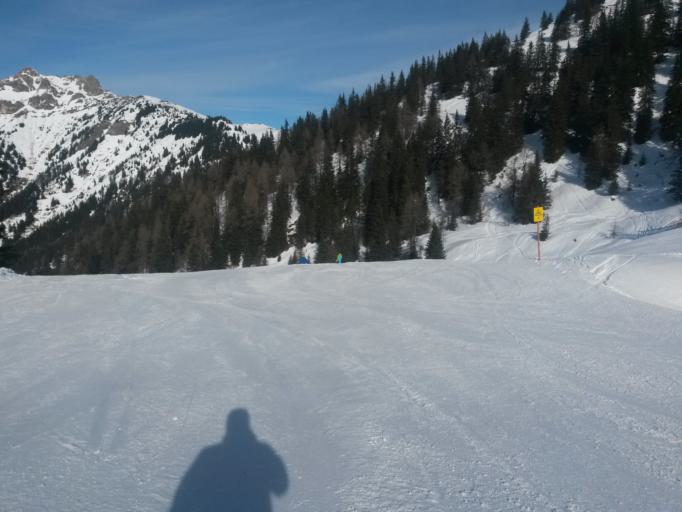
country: AT
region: Salzburg
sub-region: Politischer Bezirk Sankt Johann im Pongau
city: Dorfgastein
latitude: 47.2400
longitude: 13.1456
